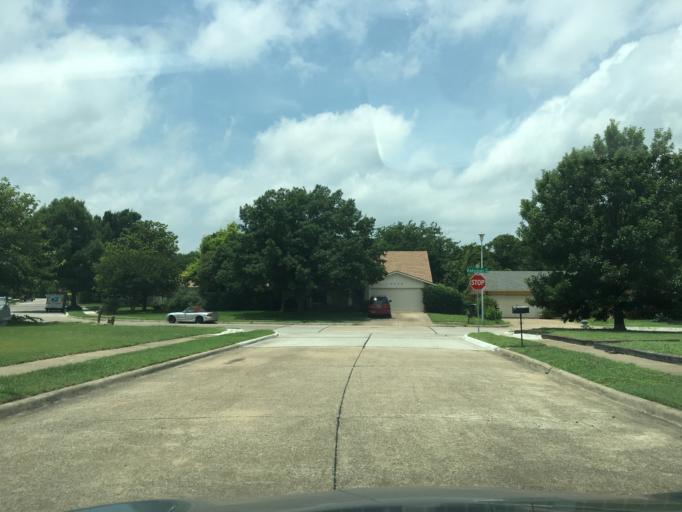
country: US
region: Texas
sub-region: Dallas County
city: Garland
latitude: 32.9290
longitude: -96.6728
